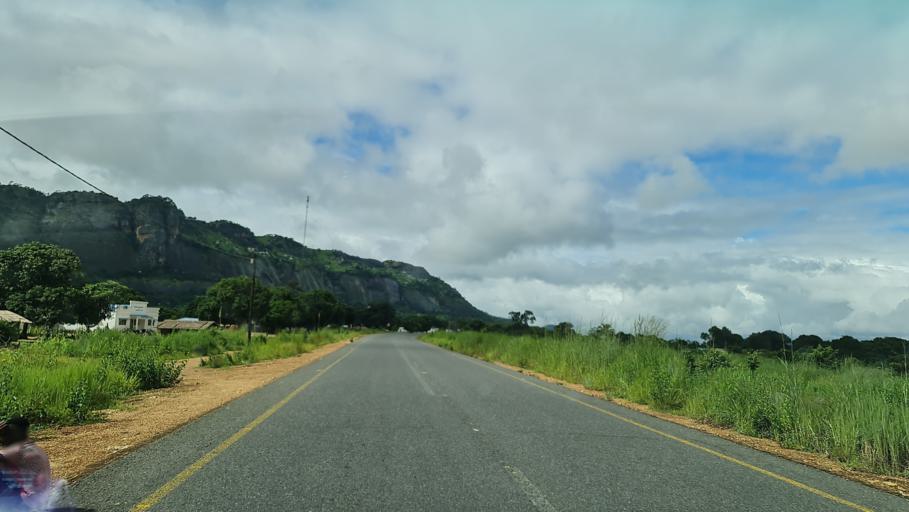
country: MZ
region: Nampula
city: Nampula
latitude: -14.9989
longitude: 38.5120
